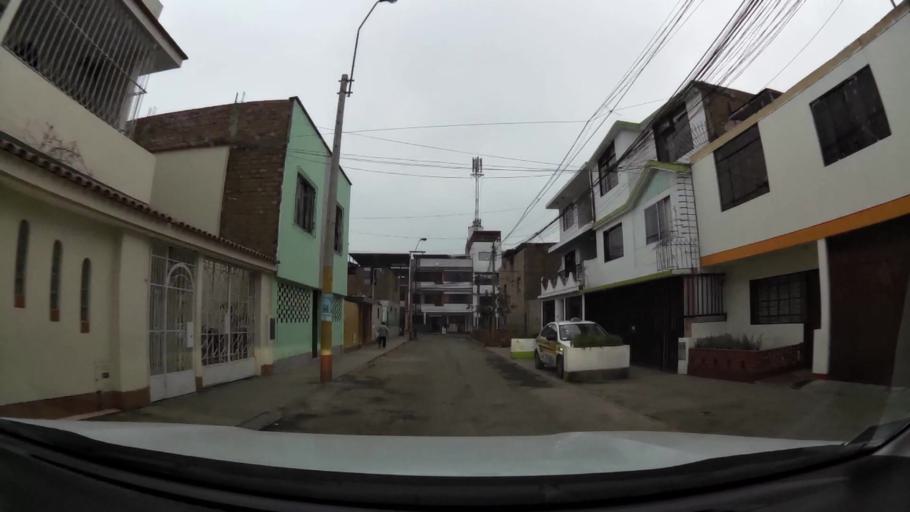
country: PE
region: Lima
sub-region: Lima
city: Surco
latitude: -12.1488
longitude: -76.9765
